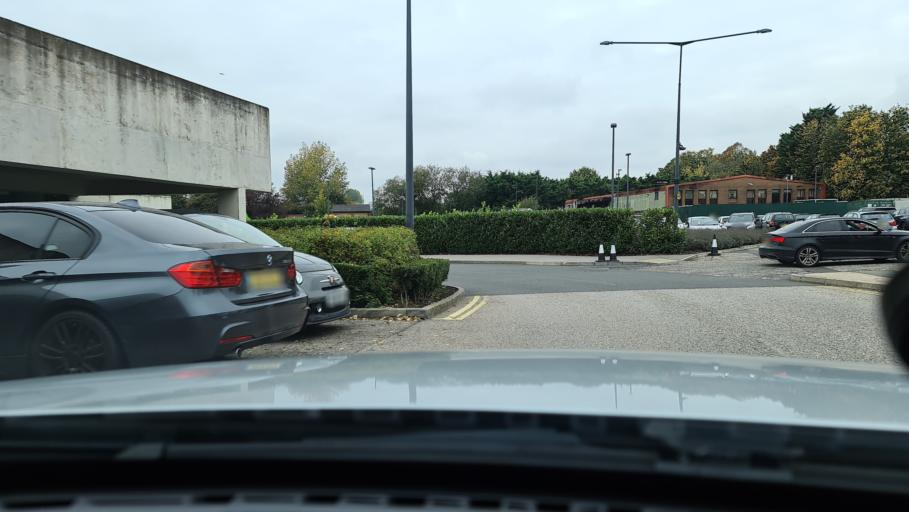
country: GB
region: England
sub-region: Oxfordshire
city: Bicester
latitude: 51.8931
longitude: -1.1507
